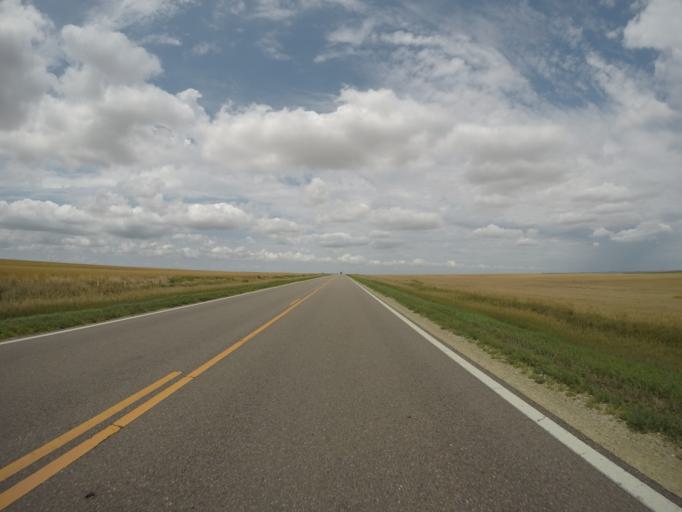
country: US
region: Kansas
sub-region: Rawlins County
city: Atwood
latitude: 39.6840
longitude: -101.0565
